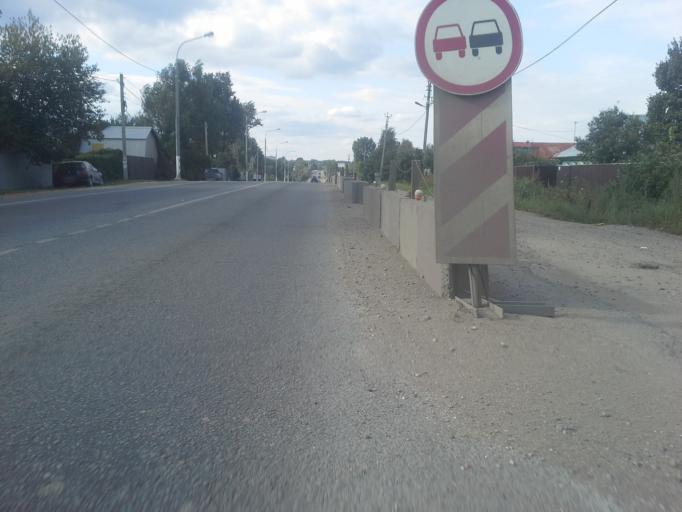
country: RU
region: Moskovskaya
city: Selyatino
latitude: 55.5418
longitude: 36.9888
